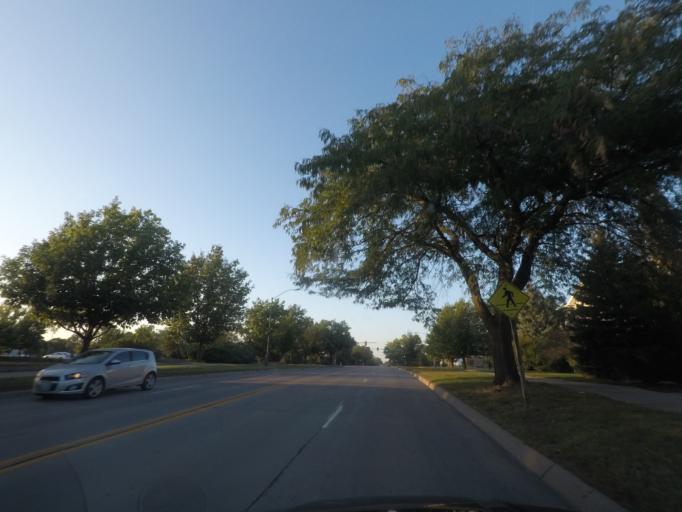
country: US
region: Iowa
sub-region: Story County
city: Ames
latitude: 42.0328
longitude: -93.6447
